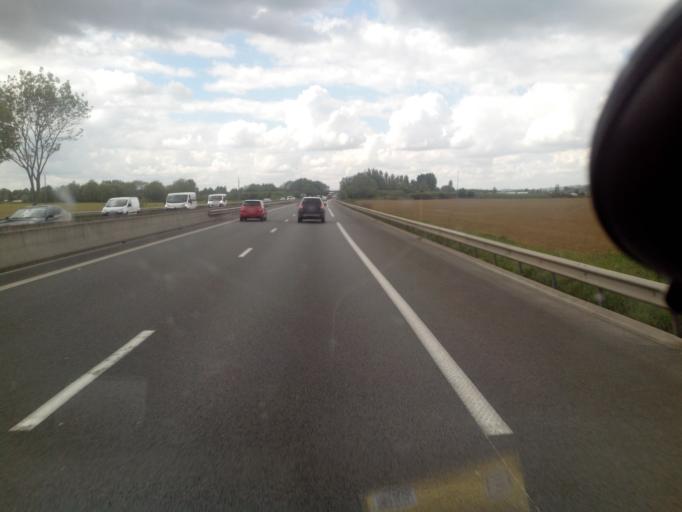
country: FR
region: Nord-Pas-de-Calais
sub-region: Departement du Nord
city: Steenwerck
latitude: 50.6979
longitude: 2.8001
